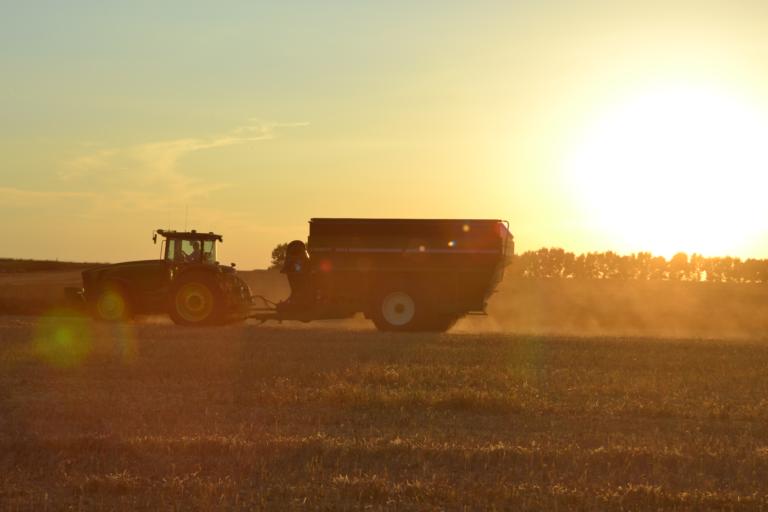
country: US
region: North Dakota
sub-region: Mercer County
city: Beulah
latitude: 47.6876
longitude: -101.9012
